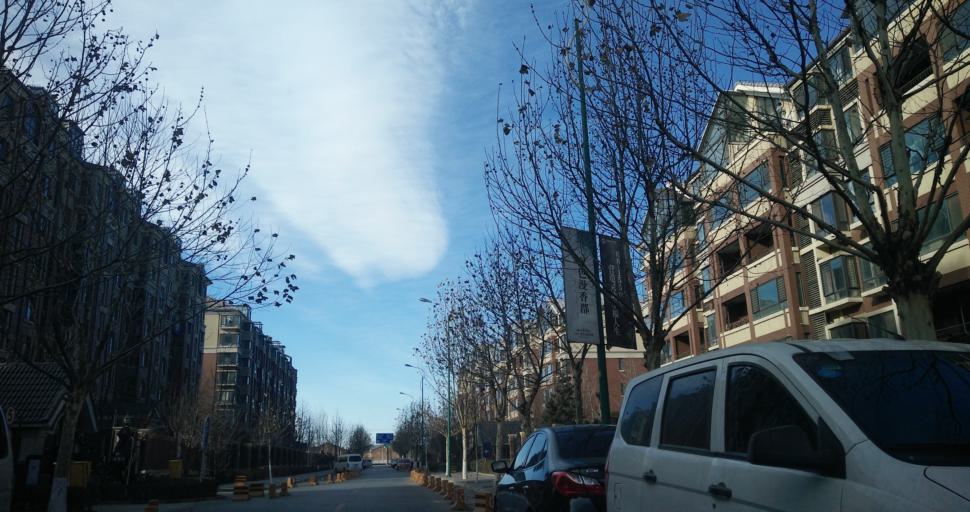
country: CN
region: Beijing
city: Xingfeng
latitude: 39.7126
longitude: 116.3944
